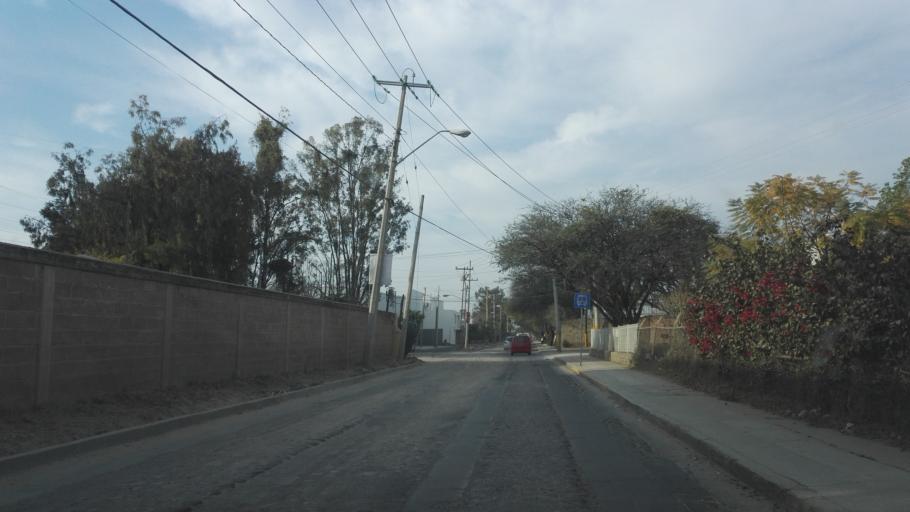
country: MX
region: Guanajuato
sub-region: Leon
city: Fraccionamiento Paraiso Real
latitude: 21.0891
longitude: -101.6103
